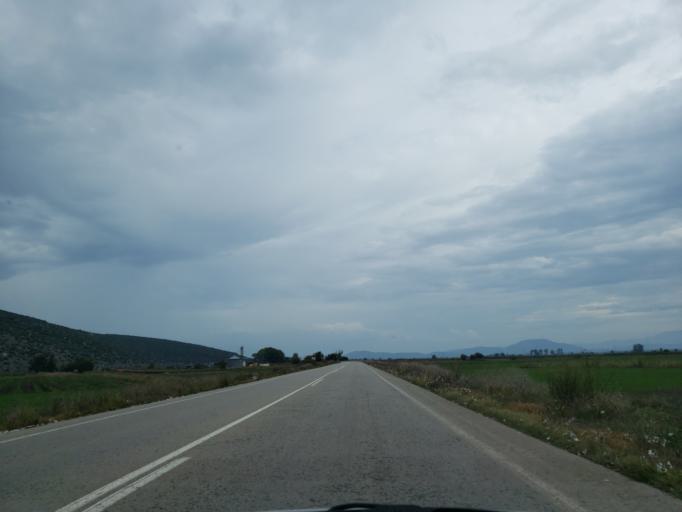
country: GR
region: Central Greece
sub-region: Nomos Voiotias
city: Orchomenos
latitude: 38.4882
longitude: 23.0661
